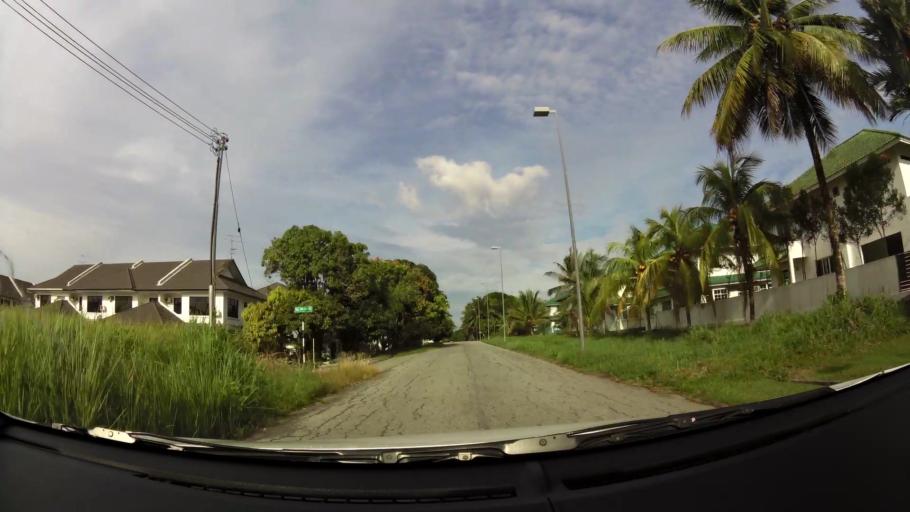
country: BN
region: Brunei and Muara
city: Bandar Seri Begawan
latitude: 4.9099
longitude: 114.8913
